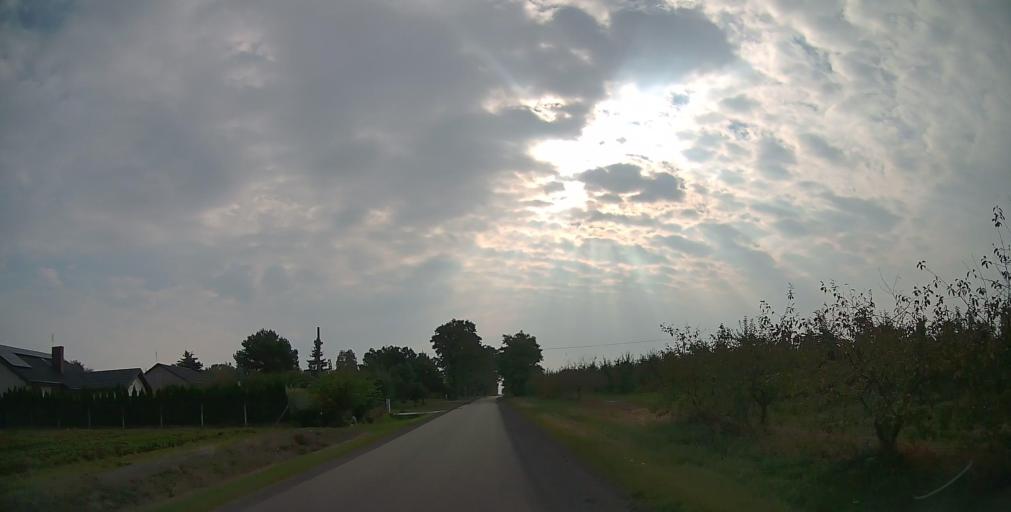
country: PL
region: Masovian Voivodeship
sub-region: Powiat grojecki
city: Mogielnica
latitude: 51.6574
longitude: 20.7164
